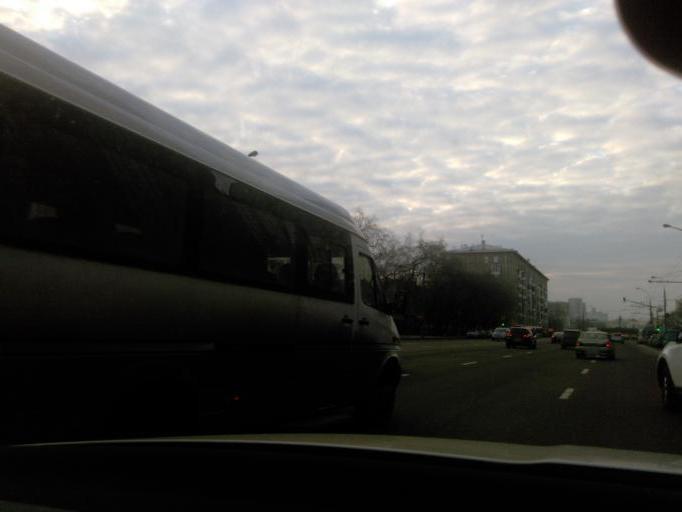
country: RU
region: Moskovskaya
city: Dorogomilovo
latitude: 55.7671
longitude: 37.5589
